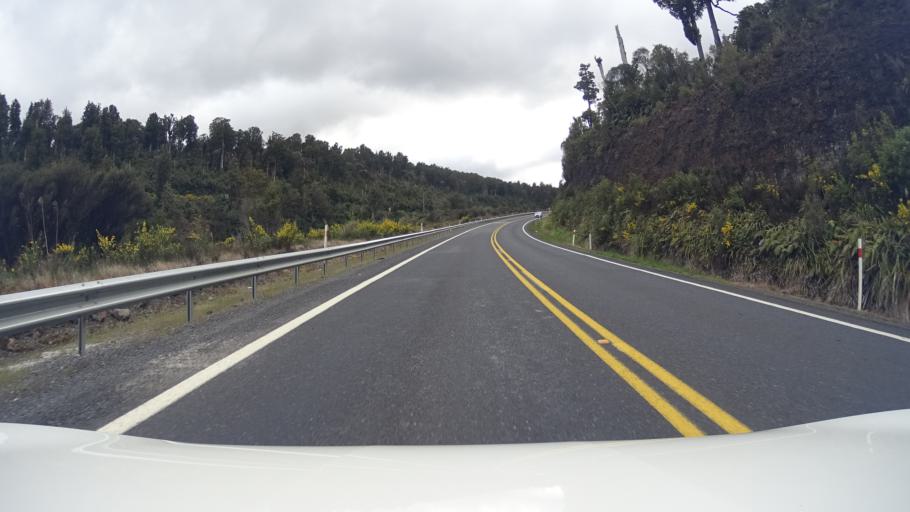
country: NZ
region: Manawatu-Wanganui
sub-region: Ruapehu District
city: Waiouru
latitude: -39.2654
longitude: 175.3936
